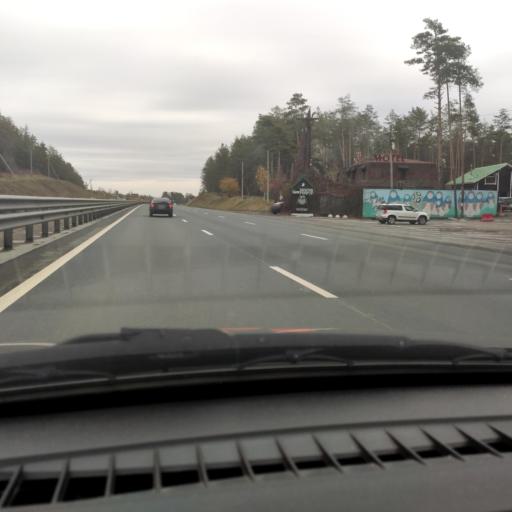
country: RU
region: Samara
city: Zhigulevsk
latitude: 53.5071
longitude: 49.5573
